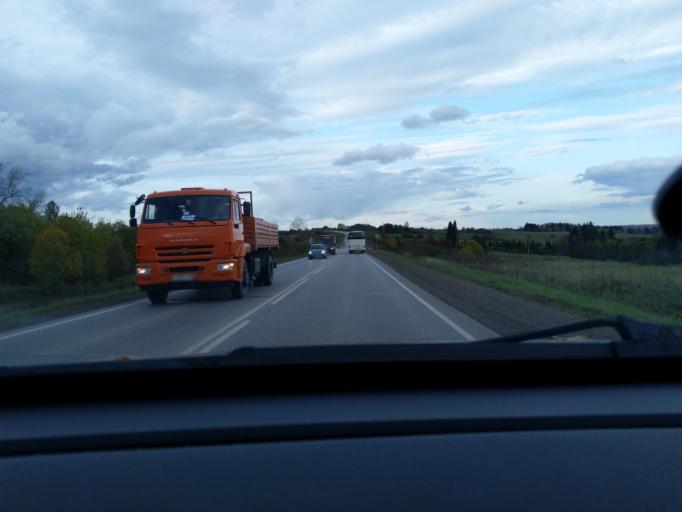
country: RU
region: Perm
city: Polazna
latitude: 58.3534
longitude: 56.4743
